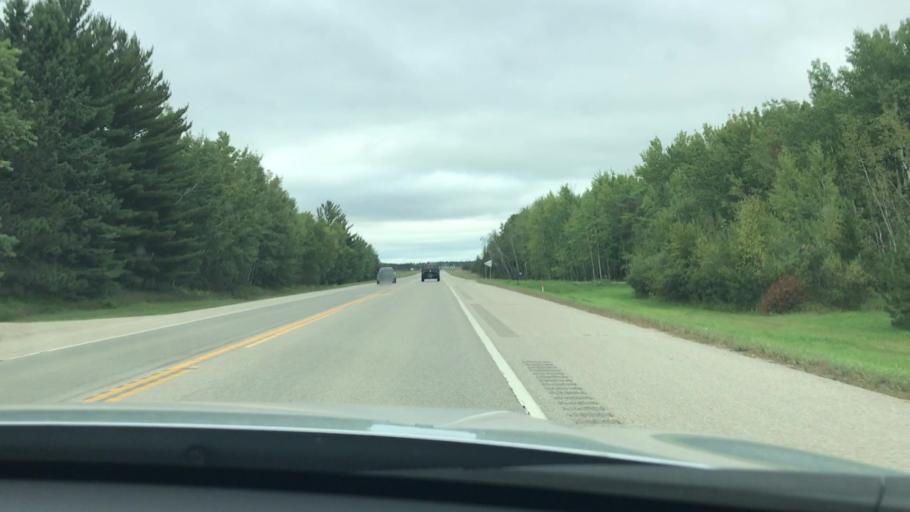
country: US
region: Minnesota
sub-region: Hubbard County
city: Park Rapids
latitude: 46.8495
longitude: -95.0796
